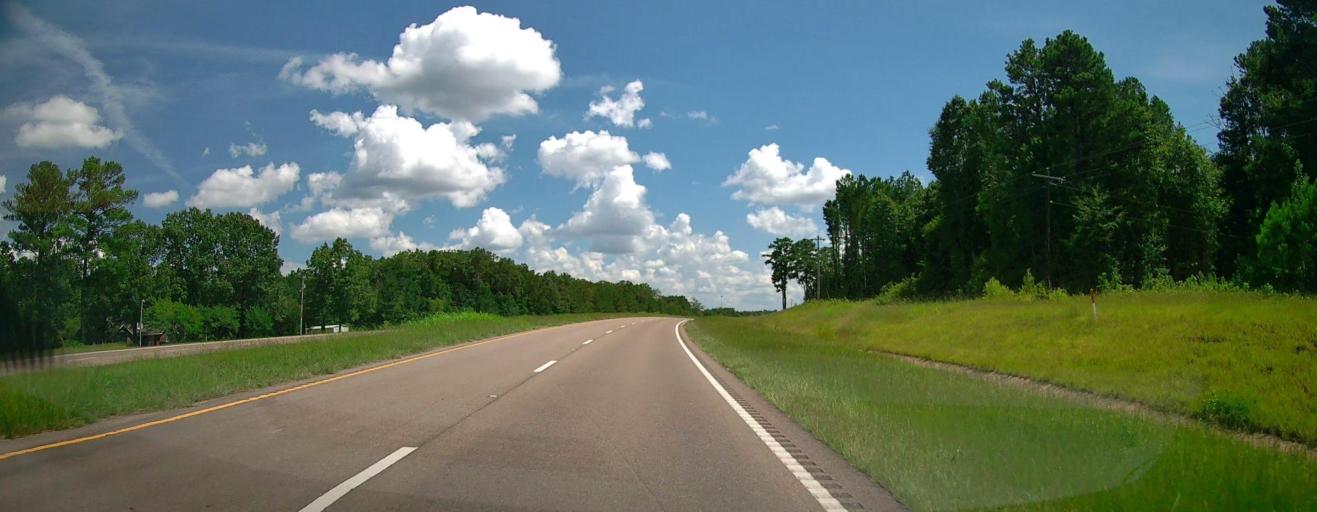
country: US
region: Mississippi
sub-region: Monroe County
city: Amory
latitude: 33.9405
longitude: -88.5984
